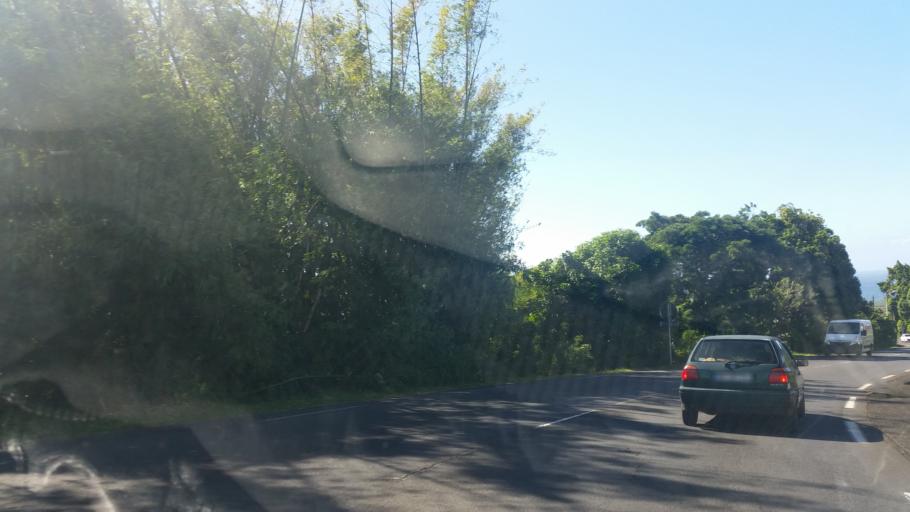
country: RE
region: Reunion
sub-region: Reunion
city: Saint-Benoit
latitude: -21.0672
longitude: 55.7048
